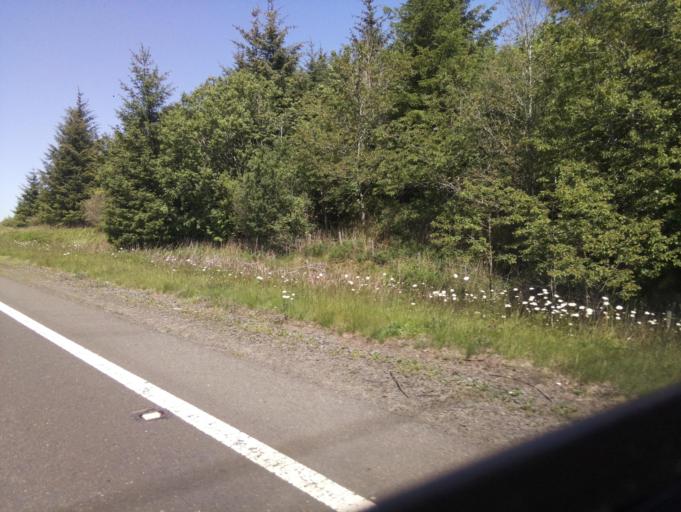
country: GB
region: Scotland
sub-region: The Scottish Borders
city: Selkirk
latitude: 55.5080
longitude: -2.8449
